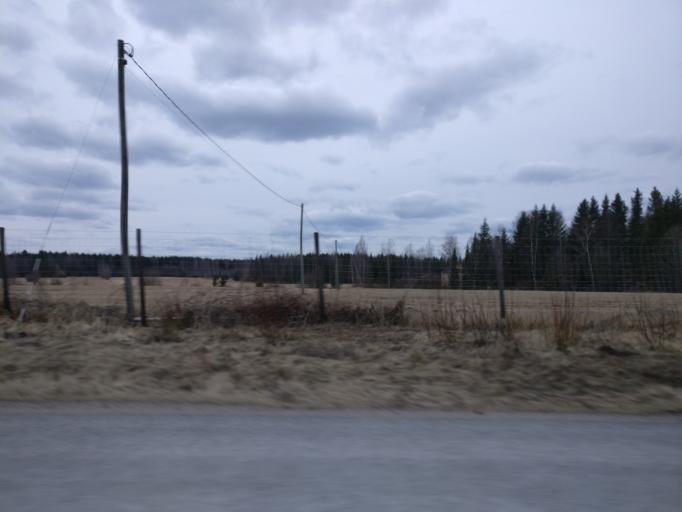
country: FI
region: Haeme
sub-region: Riihimaeki
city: Riihimaeki
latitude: 60.7256
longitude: 24.7276
